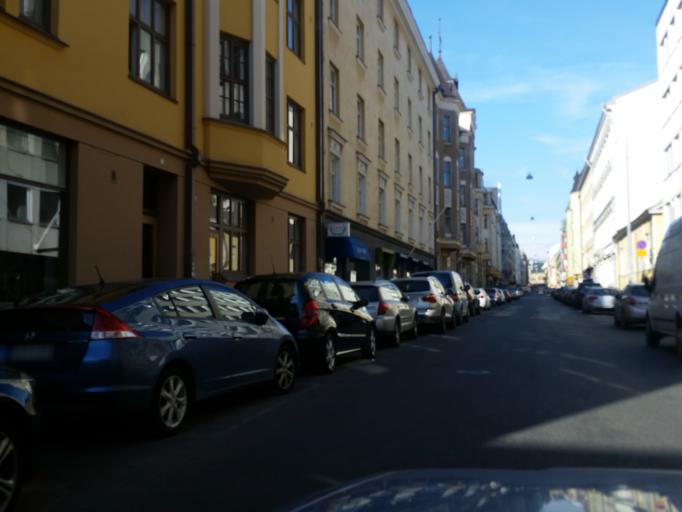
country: FI
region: Uusimaa
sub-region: Helsinki
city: Helsinki
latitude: 60.1628
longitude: 24.9359
